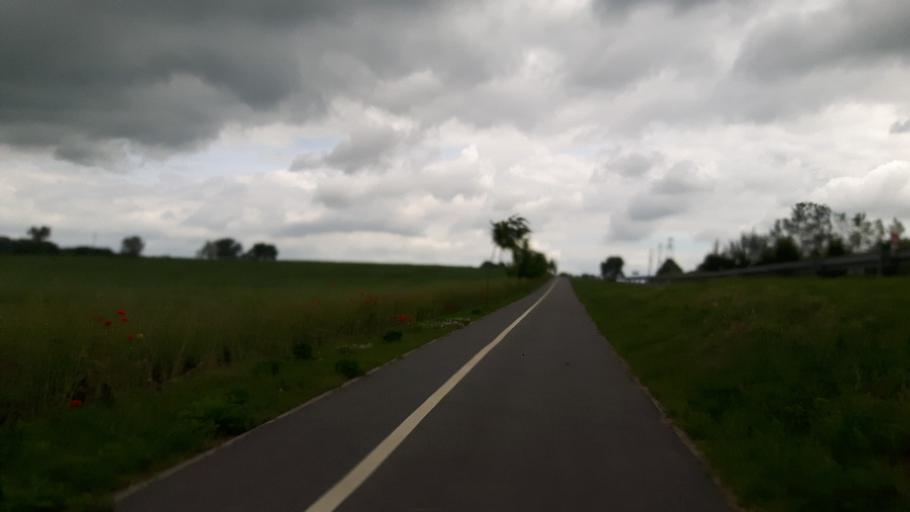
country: PL
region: West Pomeranian Voivodeship
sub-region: Powiat policki
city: Kolbaskowo
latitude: 53.3312
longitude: 14.4292
